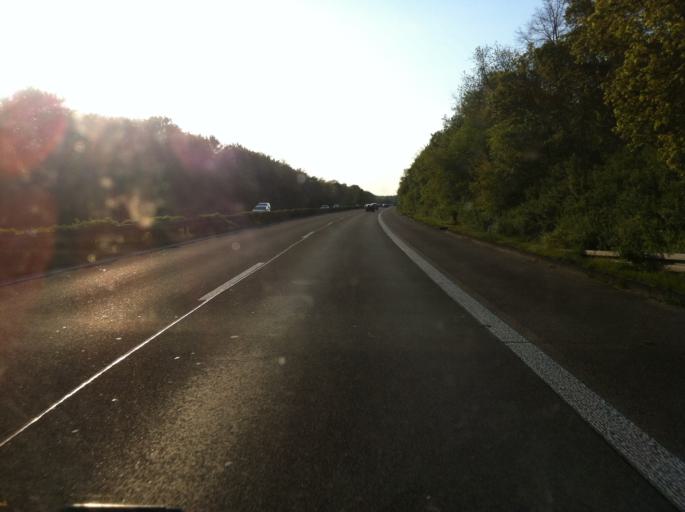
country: DE
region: North Rhine-Westphalia
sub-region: Regierungsbezirk Koln
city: Gremberghoven
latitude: 50.9087
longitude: 7.0438
